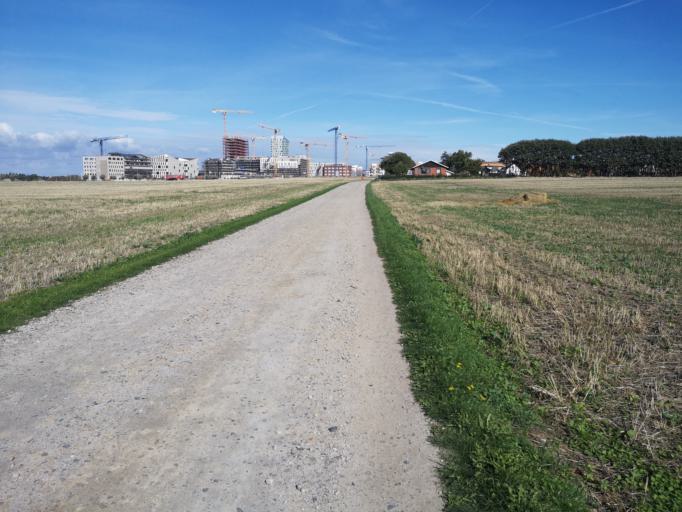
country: SE
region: Skane
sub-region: Malmo
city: Bunkeflostrand
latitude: 55.5556
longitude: 12.9786
